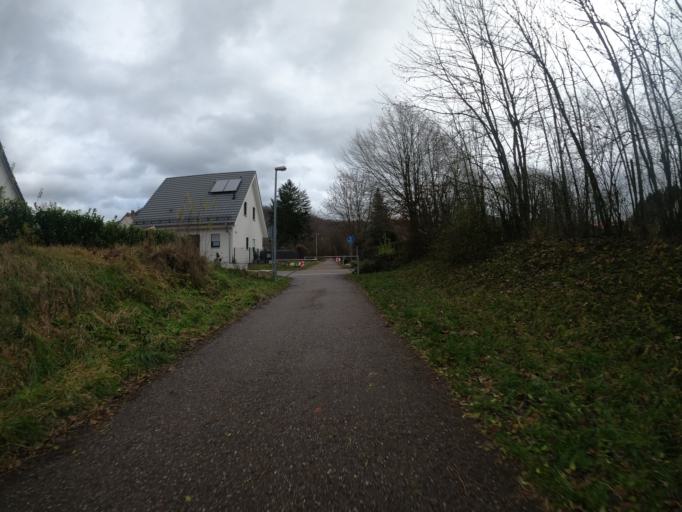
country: DE
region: Baden-Wuerttemberg
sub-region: Regierungsbezirk Stuttgart
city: Donzdorf
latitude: 48.6835
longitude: 9.8106
